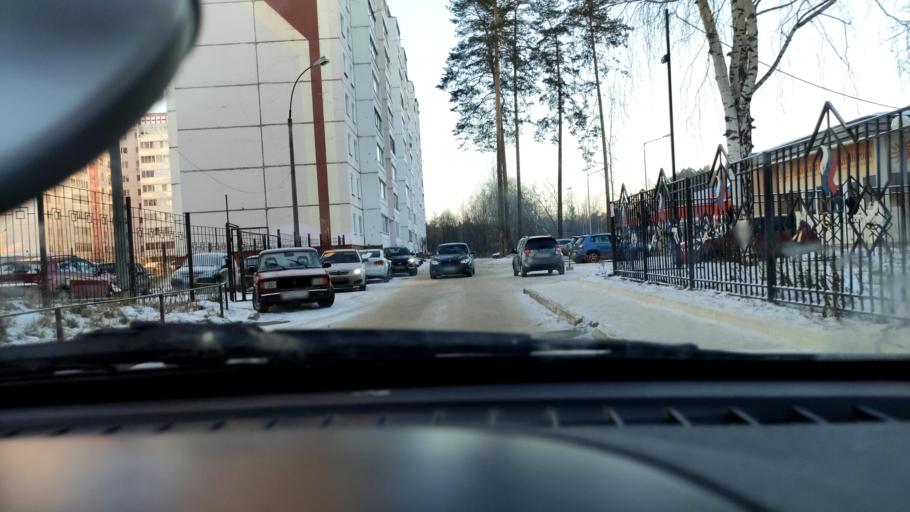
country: RU
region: Perm
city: Kondratovo
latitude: 58.0185
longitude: 55.9813
